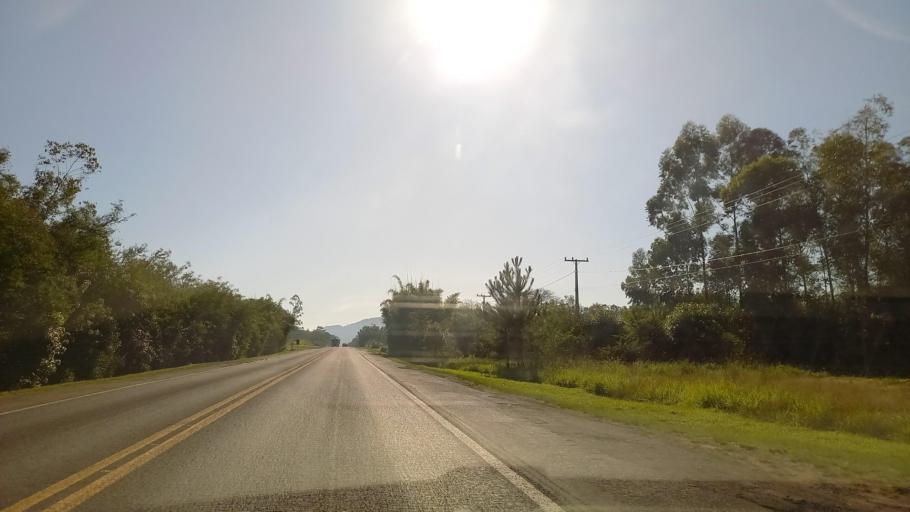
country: BR
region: Rio Grande do Sul
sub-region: Taquari
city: Taquari
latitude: -29.6990
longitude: -51.7509
